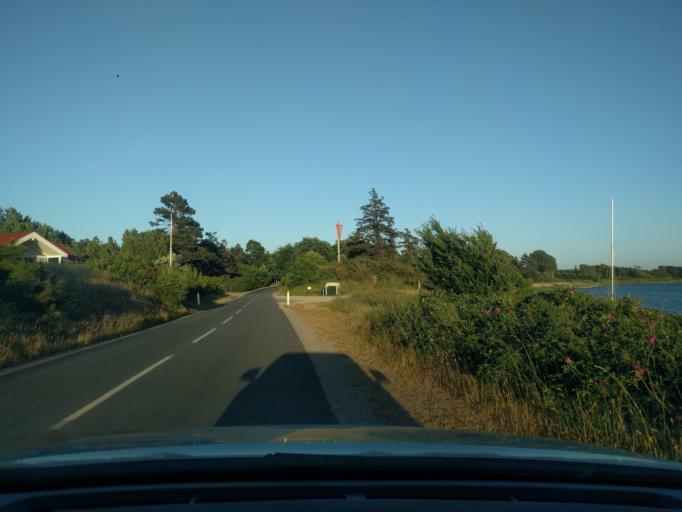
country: DK
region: South Denmark
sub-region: Kerteminde Kommune
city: Munkebo
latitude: 55.6087
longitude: 10.6159
